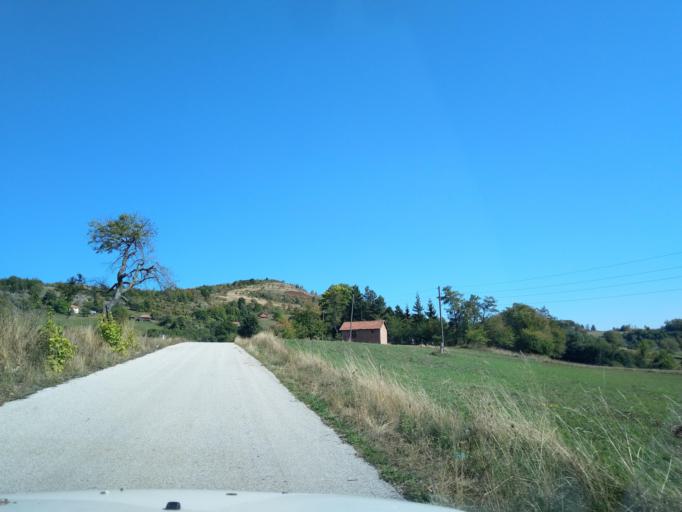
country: RS
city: Sokolovica
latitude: 43.2524
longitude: 20.3147
